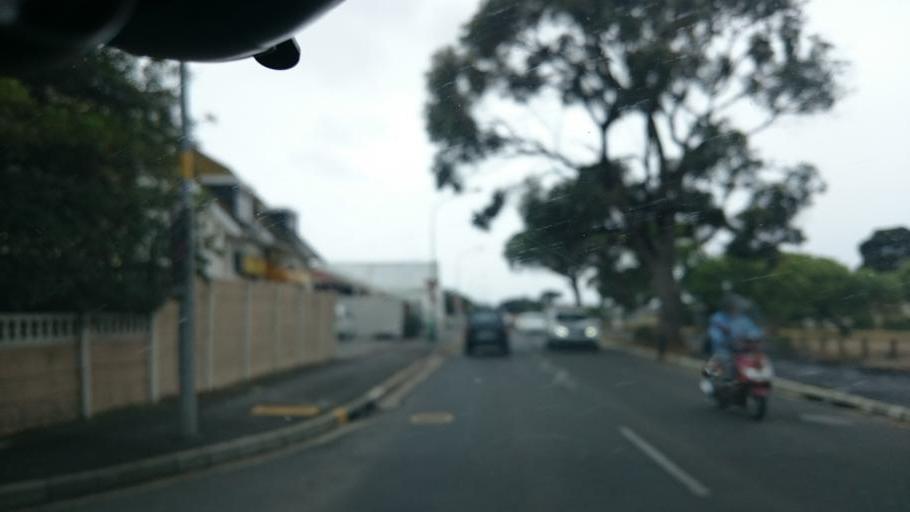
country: ZA
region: Western Cape
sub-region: City of Cape Town
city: Bergvliet
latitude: -34.0343
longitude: 18.4624
